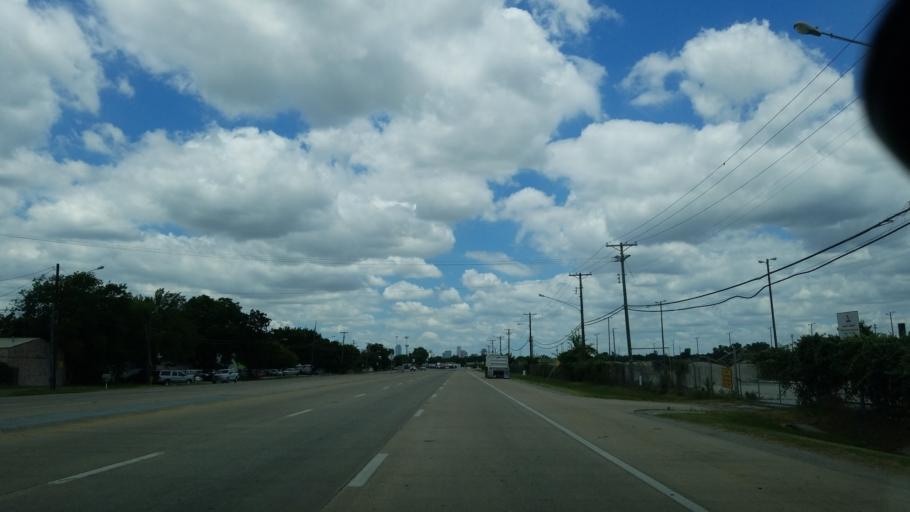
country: US
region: Texas
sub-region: Dallas County
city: Hutchins
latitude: 32.7165
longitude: -96.7557
